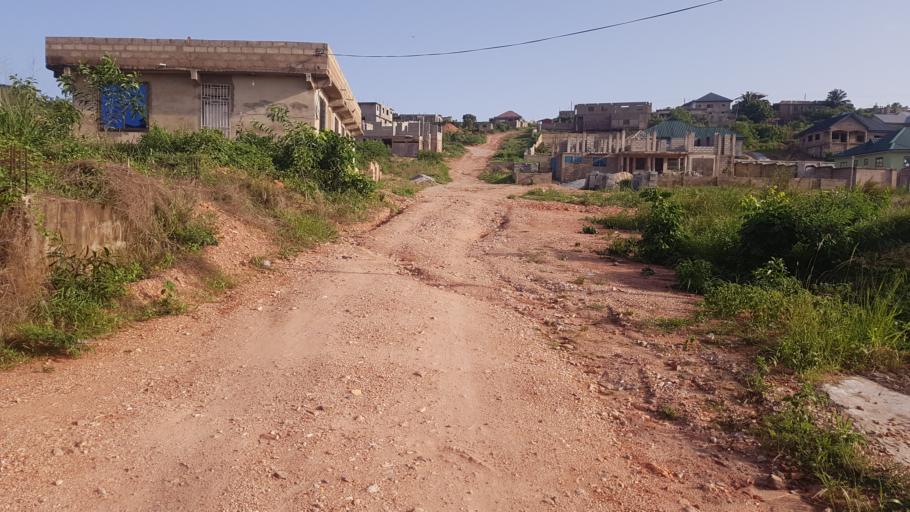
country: GH
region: Greater Accra
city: Gbawe
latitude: 5.5217
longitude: -0.3388
